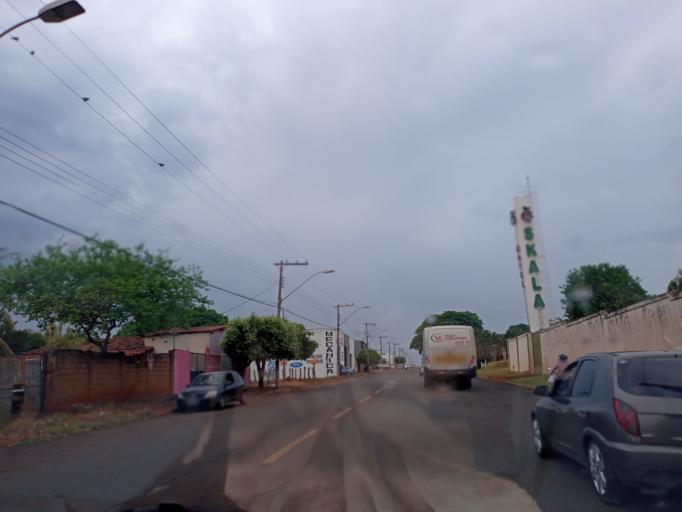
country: BR
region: Minas Gerais
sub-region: Ituiutaba
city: Ituiutaba
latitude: -18.9856
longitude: -49.4838
